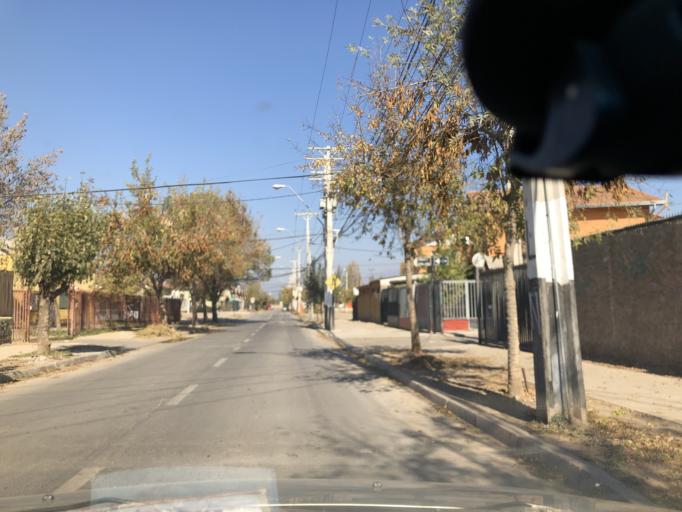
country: CL
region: Santiago Metropolitan
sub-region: Provincia de Cordillera
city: Puente Alto
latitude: -33.6304
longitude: -70.5949
